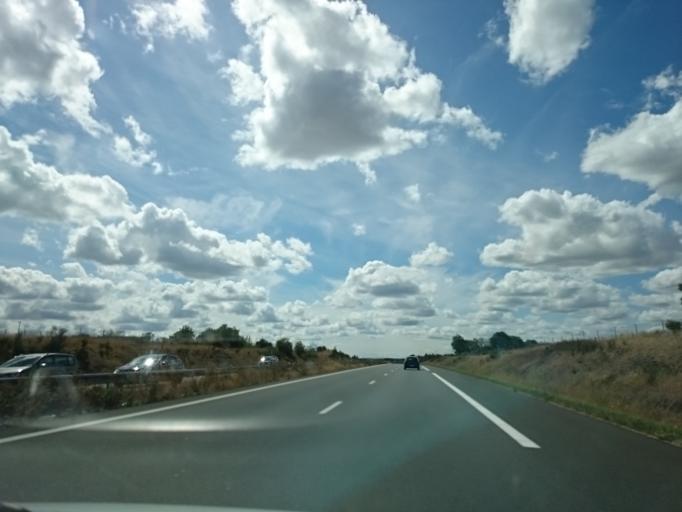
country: FR
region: Pays de la Loire
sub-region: Departement de la Loire-Atlantique
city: Saint-Herblon
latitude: 47.4134
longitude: -1.1441
